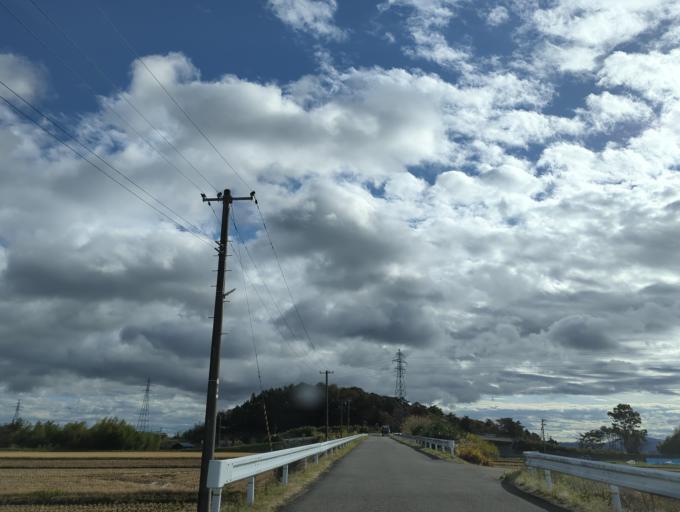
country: JP
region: Fukushima
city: Koriyama
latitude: 37.4096
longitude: 140.3173
